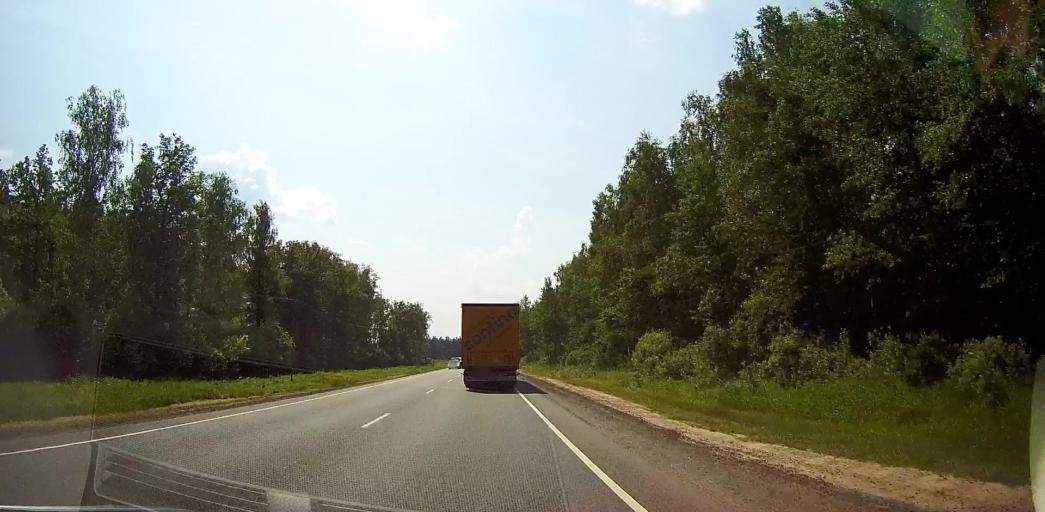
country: RU
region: Moskovskaya
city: Meshcherino
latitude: 55.2087
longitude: 38.3835
